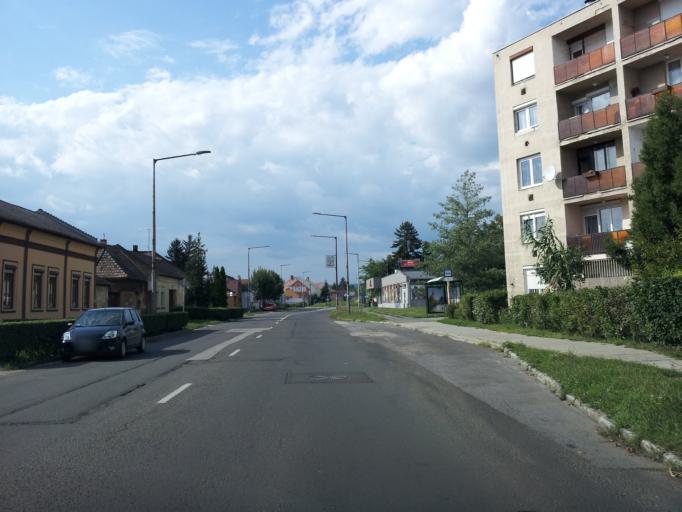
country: HU
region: Pest
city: Vac
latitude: 47.7903
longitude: 19.1175
